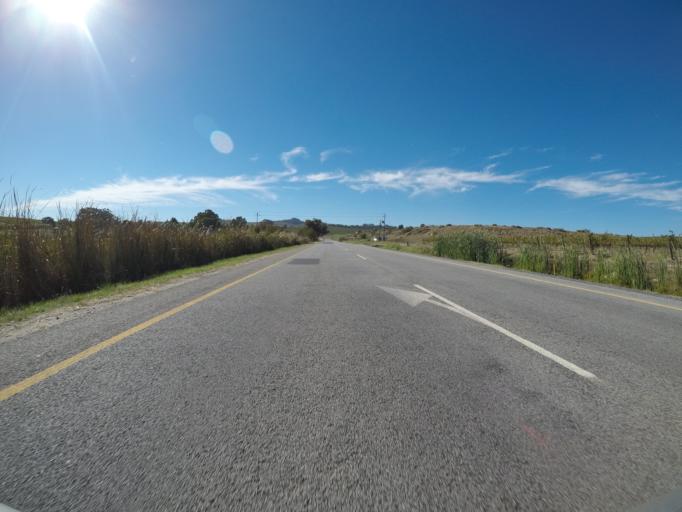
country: ZA
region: Western Cape
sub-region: Cape Winelands District Municipality
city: Stellenbosch
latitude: -33.9805
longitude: 18.7540
